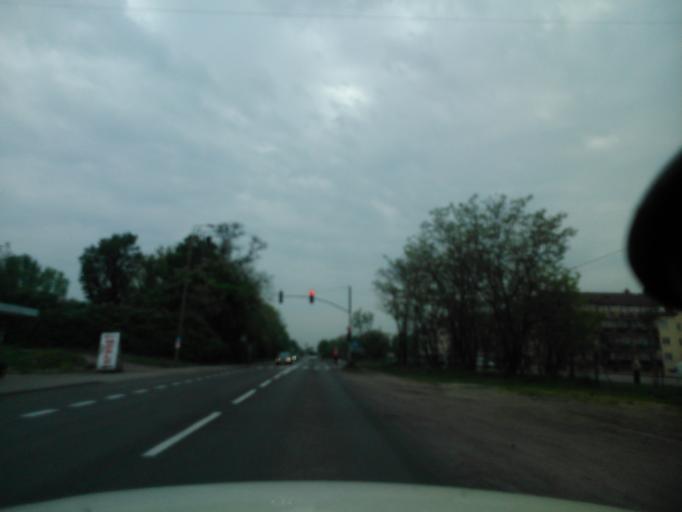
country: PL
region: Kujawsko-Pomorskie
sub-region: Powiat torunski
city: Lubicz Dolny
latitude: 53.0487
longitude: 18.7040
